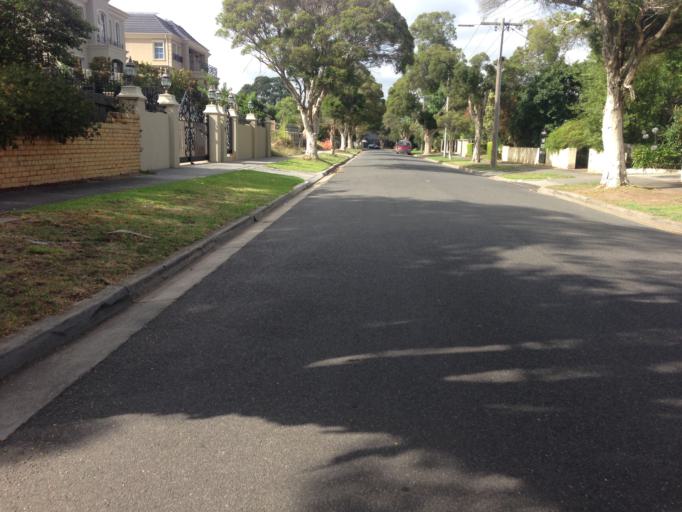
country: AU
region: Victoria
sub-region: Boroondara
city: Balwyn North
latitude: -37.7971
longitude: 145.0857
